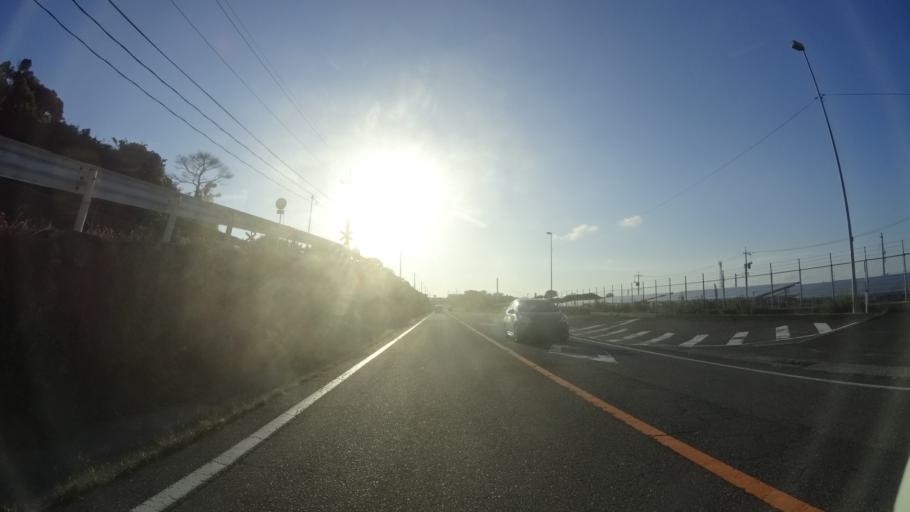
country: JP
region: Tottori
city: Yonago
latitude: 35.5139
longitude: 133.5236
